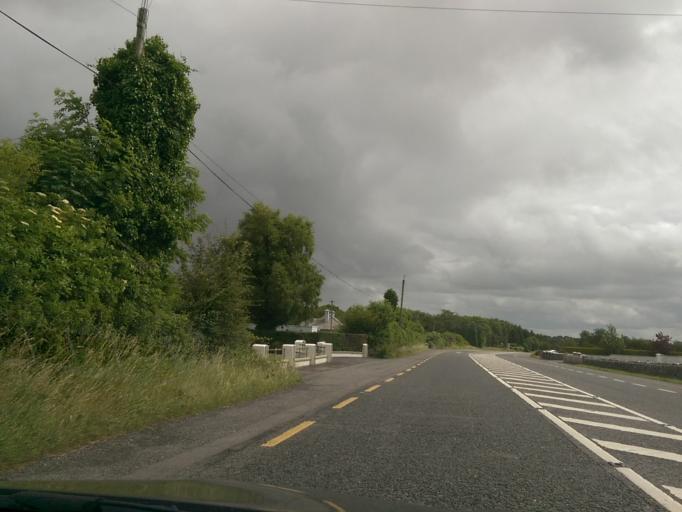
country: IE
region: Connaught
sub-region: County Galway
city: Loughrea
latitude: 53.2127
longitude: -8.5040
